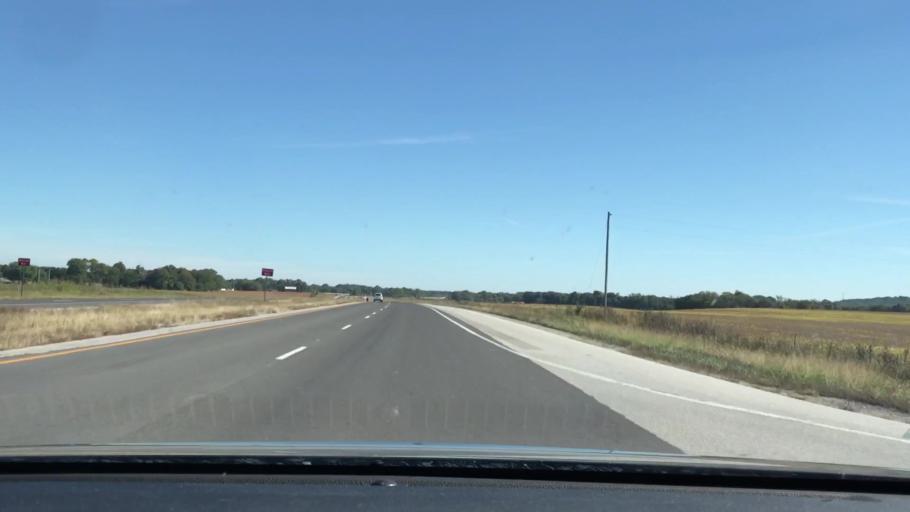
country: US
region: Kentucky
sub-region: Logan County
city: Russellville
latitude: 36.8253
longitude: -86.9852
